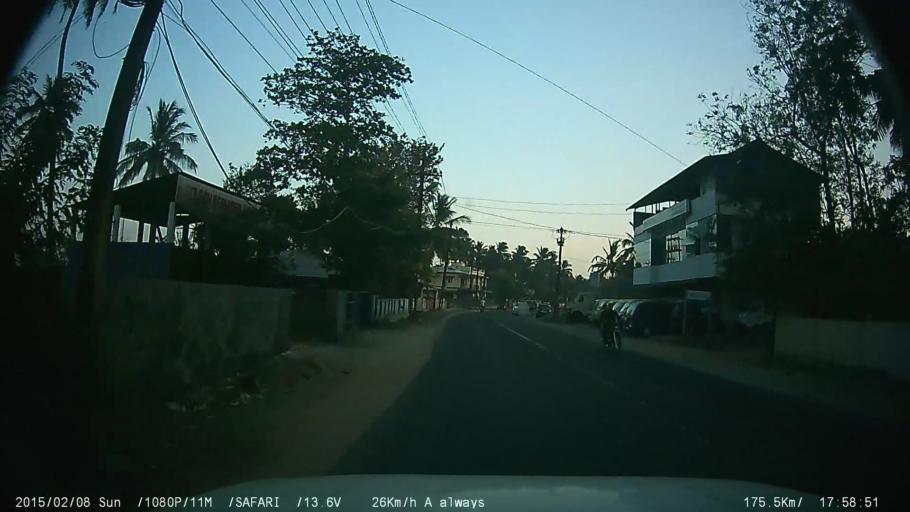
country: IN
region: Kerala
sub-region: Palakkad district
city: Palakkad
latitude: 10.7593
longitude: 76.6521
